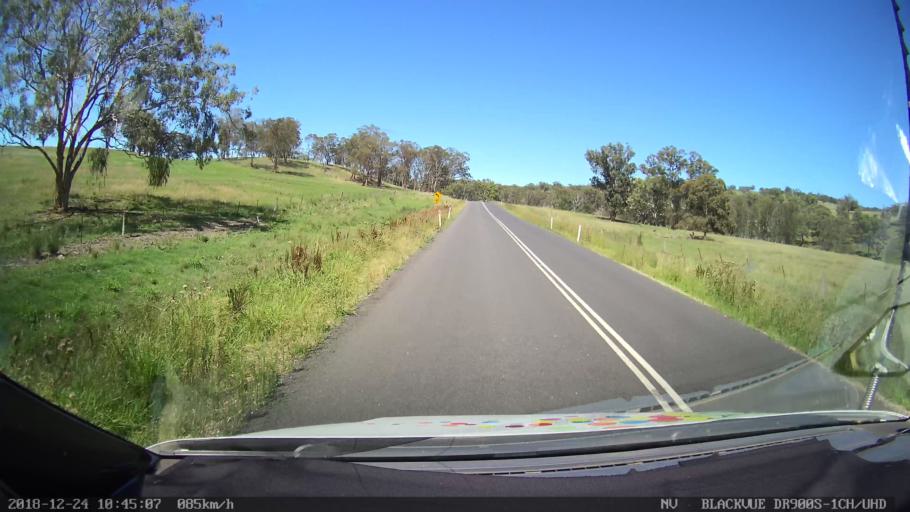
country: AU
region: New South Wales
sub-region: Upper Hunter Shire
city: Merriwa
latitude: -31.8997
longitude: 150.4384
